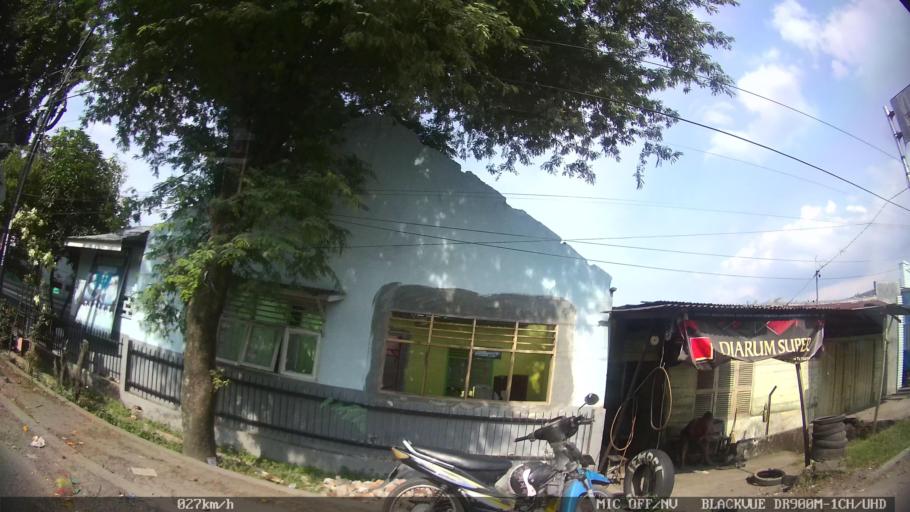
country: ID
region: North Sumatra
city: Binjai
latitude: 3.6182
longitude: 98.4967
